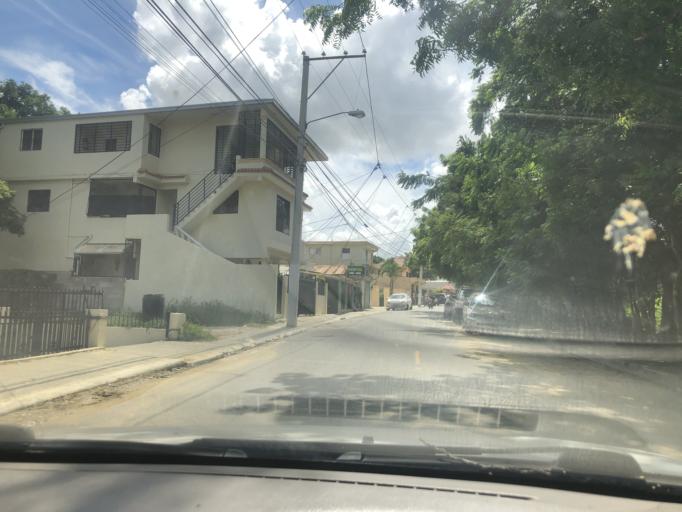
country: DO
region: Santiago
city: Santiago de los Caballeros
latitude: 19.4107
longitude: -70.7081
